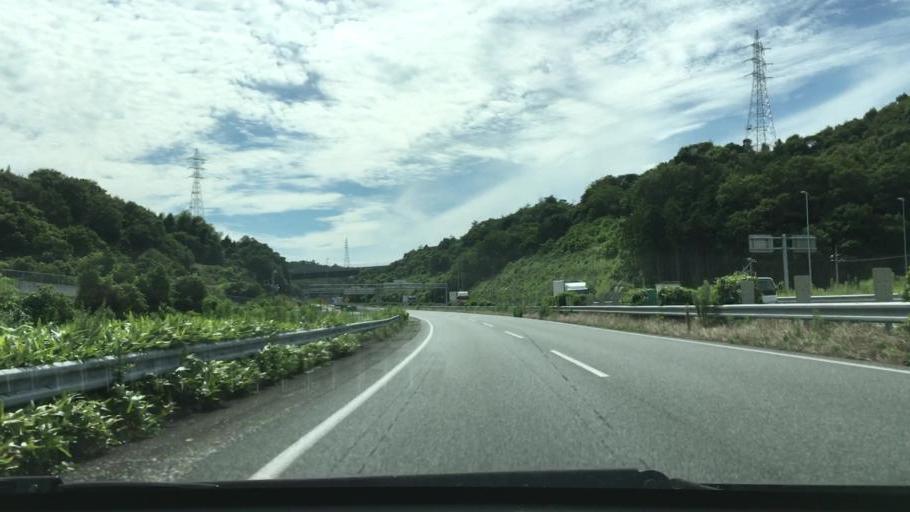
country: JP
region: Yamaguchi
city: Ogori-shimogo
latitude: 34.1266
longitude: 131.4017
